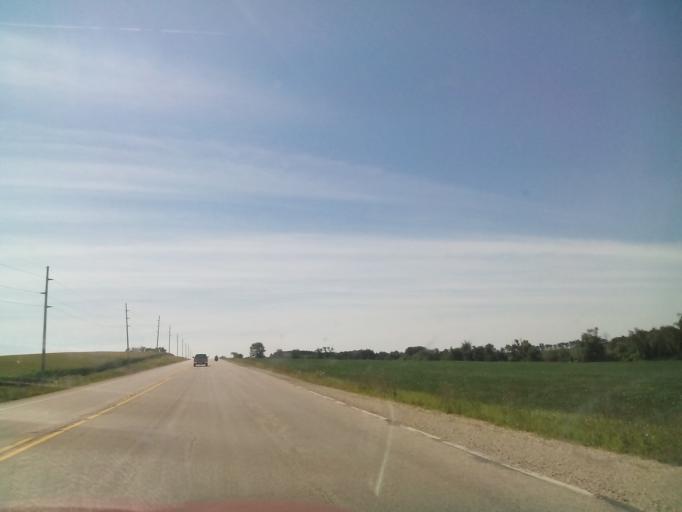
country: US
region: Wisconsin
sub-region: Green County
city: Monticello
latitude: 42.6947
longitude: -89.6169
